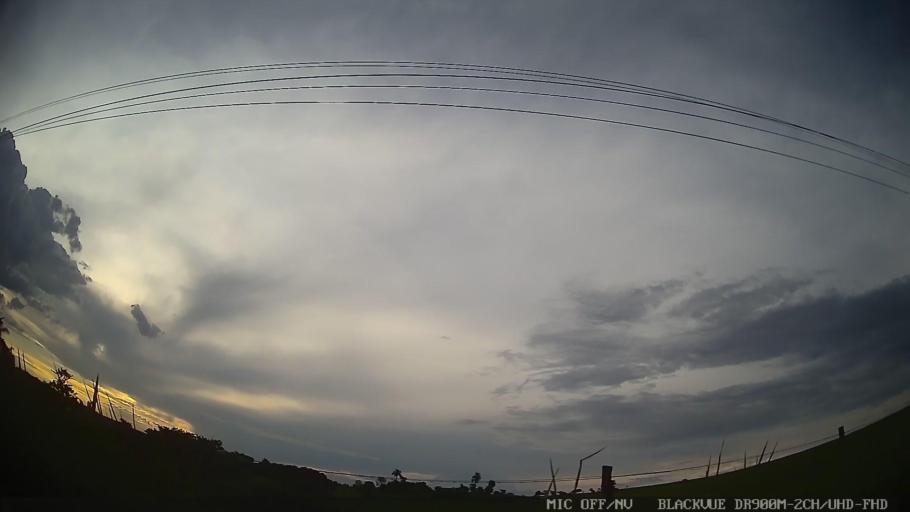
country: BR
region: Sao Paulo
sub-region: Jaguariuna
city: Jaguariuna
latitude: -22.7307
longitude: -47.0026
